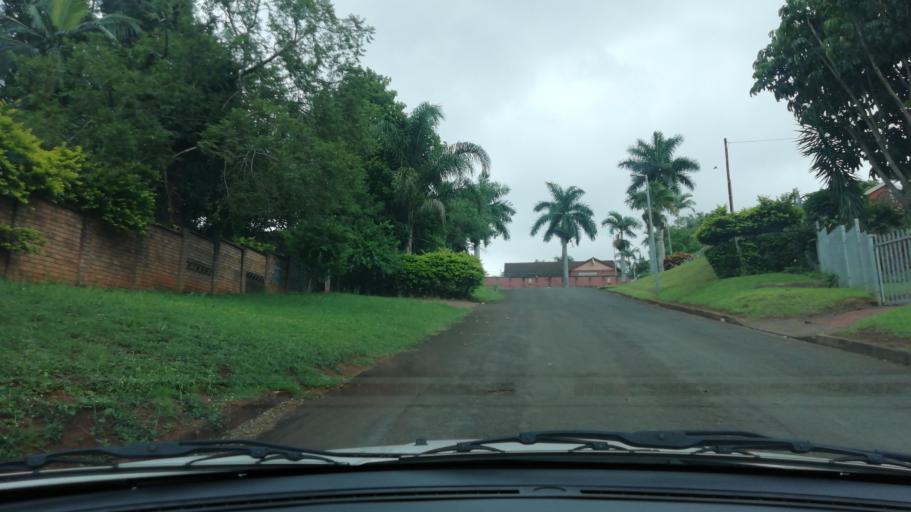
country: ZA
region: KwaZulu-Natal
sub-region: uThungulu District Municipality
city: Empangeni
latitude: -28.7680
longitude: 31.9005
